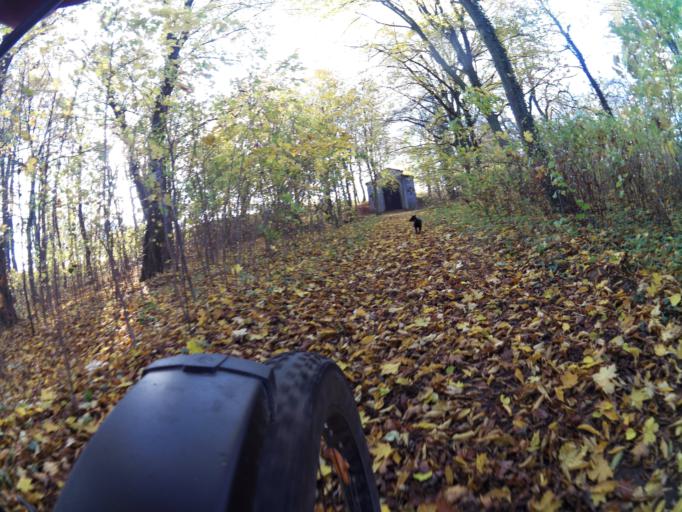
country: PL
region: Pomeranian Voivodeship
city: Strzelno
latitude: 54.7578
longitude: 18.2912
